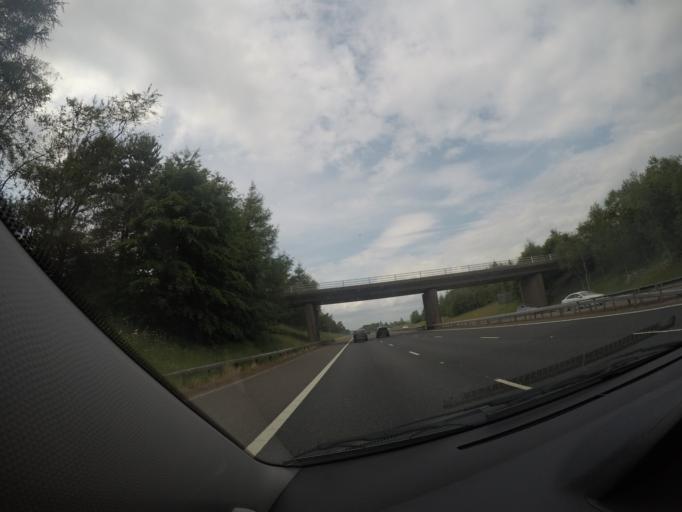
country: GB
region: Scotland
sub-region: Dumfries and Galloway
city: Lockerbie
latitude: 55.1235
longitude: -3.3644
